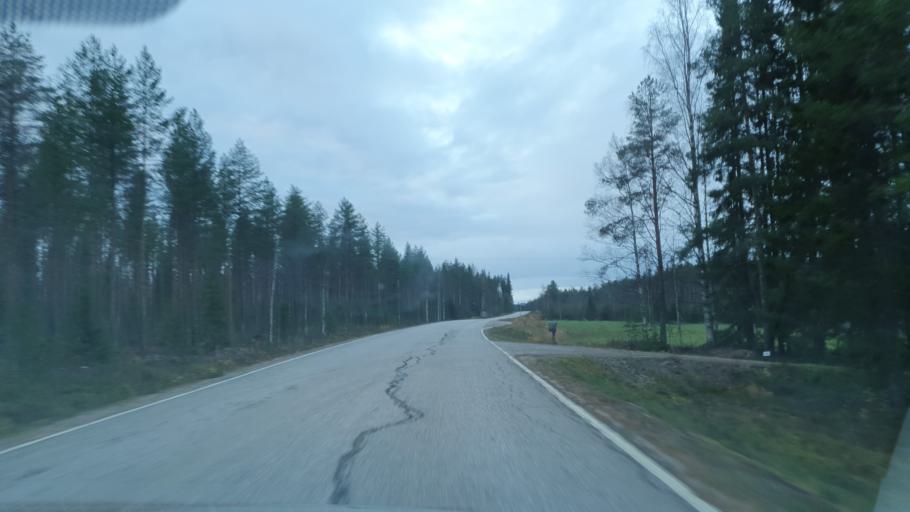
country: FI
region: Kainuu
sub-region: Kajaani
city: Ristijaervi
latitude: 64.4223
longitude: 28.4032
